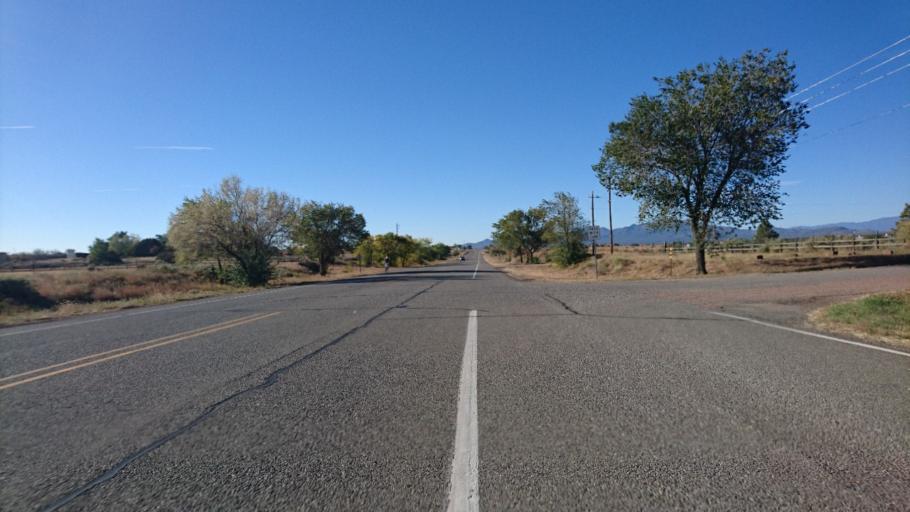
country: US
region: New Mexico
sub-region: Santa Fe County
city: La Cienega
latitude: 35.5006
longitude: -106.0641
